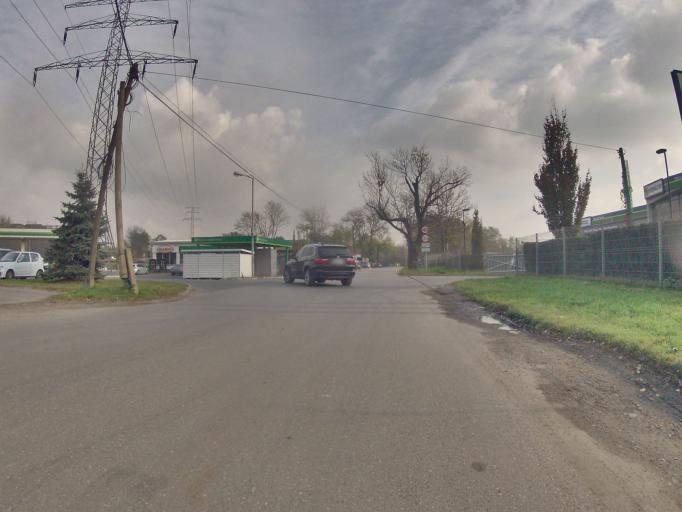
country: PL
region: Lesser Poland Voivodeship
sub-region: Powiat wielicki
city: Wegrzce Wielkie
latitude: 50.0700
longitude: 20.1009
